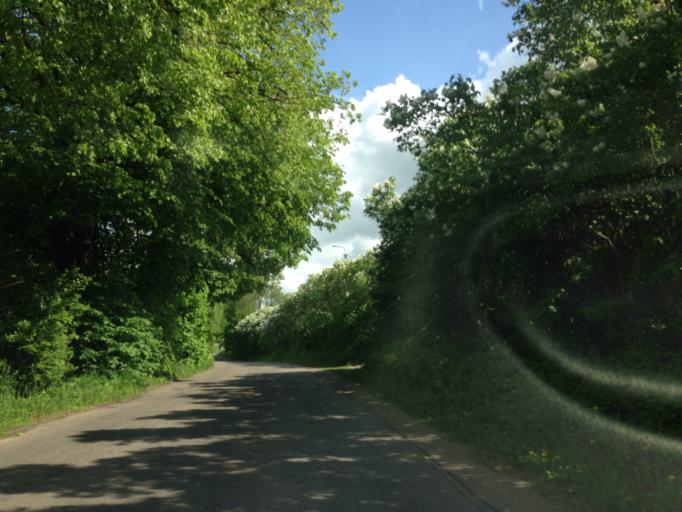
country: PL
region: Warmian-Masurian Voivodeship
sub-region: Powiat nidzicki
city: Kozlowo
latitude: 53.4160
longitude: 20.2599
